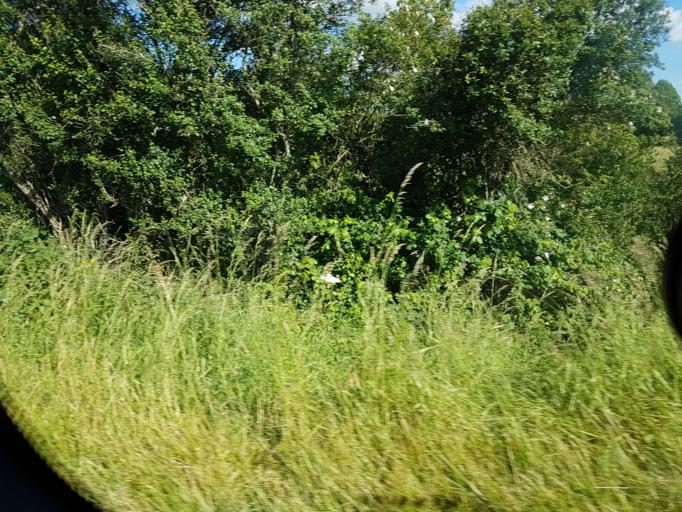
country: FR
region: Bourgogne
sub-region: Departement de Saone-et-Loire
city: Epinac
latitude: 46.9941
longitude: 4.5043
